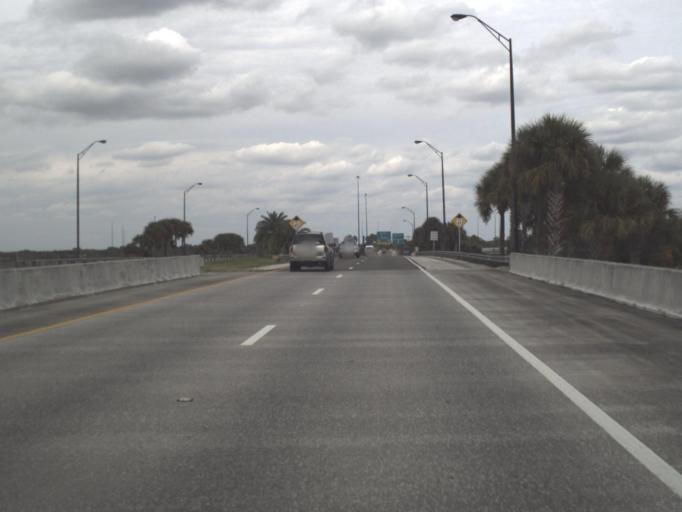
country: US
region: Florida
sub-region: Polk County
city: Winston
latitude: 28.0294
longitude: -82.0400
